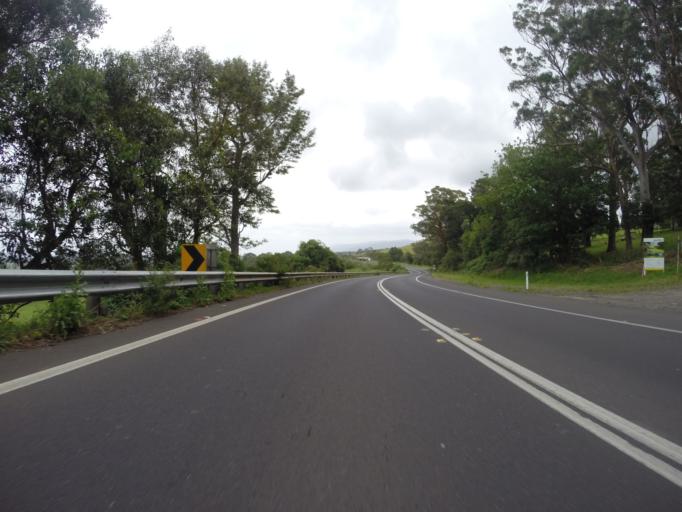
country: AU
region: New South Wales
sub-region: Shoalhaven Shire
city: Berry
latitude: -34.7567
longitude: 150.7481
